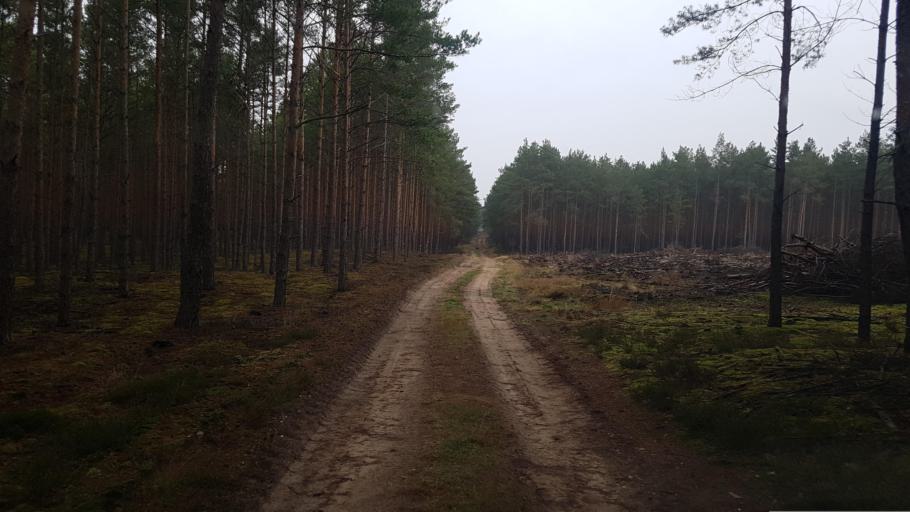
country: DE
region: Brandenburg
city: Sallgast
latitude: 51.6443
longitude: 13.8144
